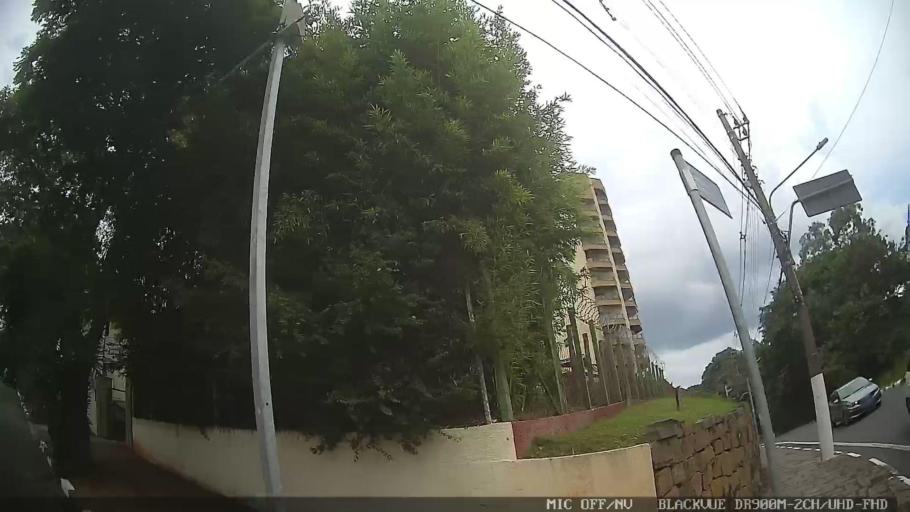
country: BR
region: Sao Paulo
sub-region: Atibaia
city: Atibaia
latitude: -23.1174
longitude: -46.5491
